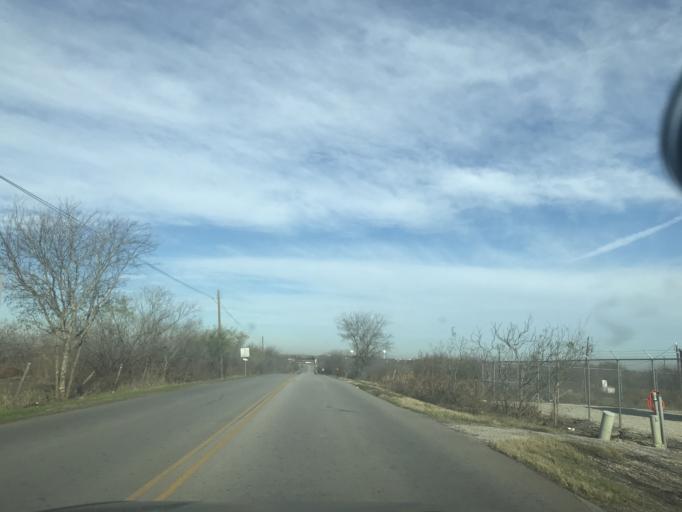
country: US
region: Texas
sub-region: Travis County
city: Manor
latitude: 30.3307
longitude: -97.5479
